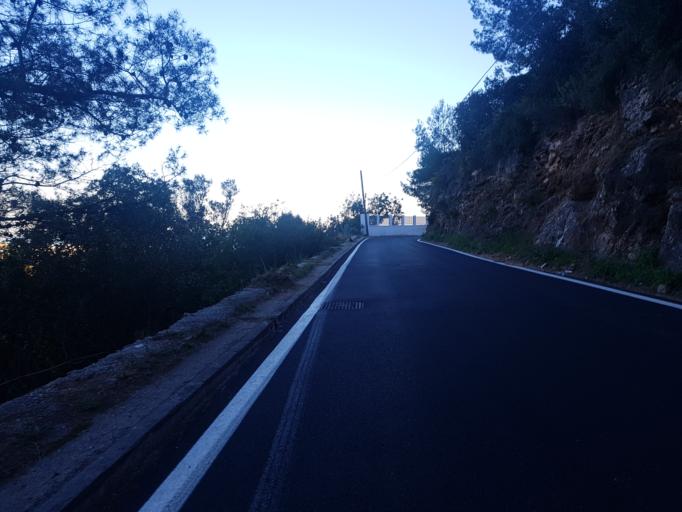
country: ES
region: Andalusia
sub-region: Provincia de Malaga
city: Marbella
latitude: 36.5289
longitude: -4.8857
